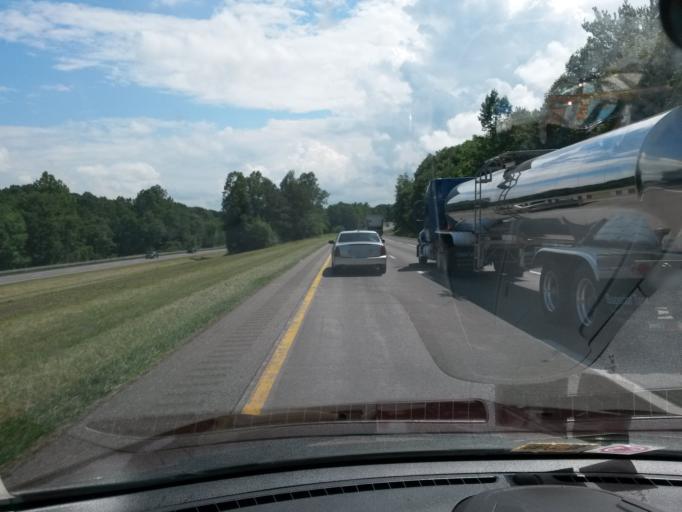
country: US
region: North Carolina
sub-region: Surry County
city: Dobson
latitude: 36.3789
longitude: -80.7907
